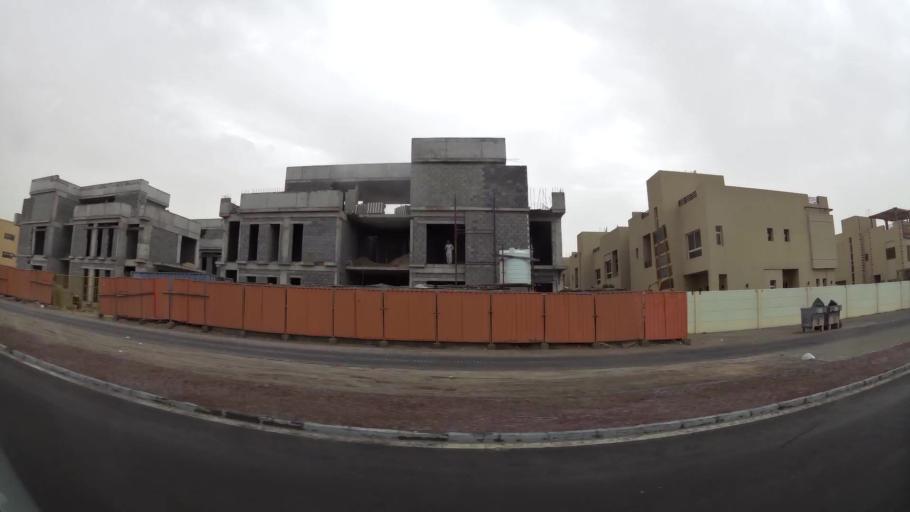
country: AE
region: Abu Dhabi
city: Abu Dhabi
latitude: 24.4393
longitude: 54.5956
